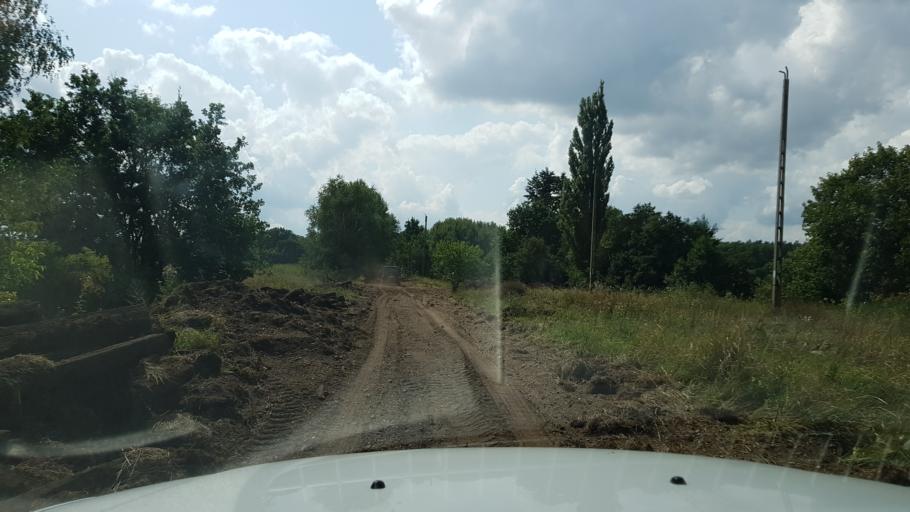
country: PL
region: West Pomeranian Voivodeship
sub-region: Powiat choszczenski
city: Pelczyce
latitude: 53.0889
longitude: 15.3055
